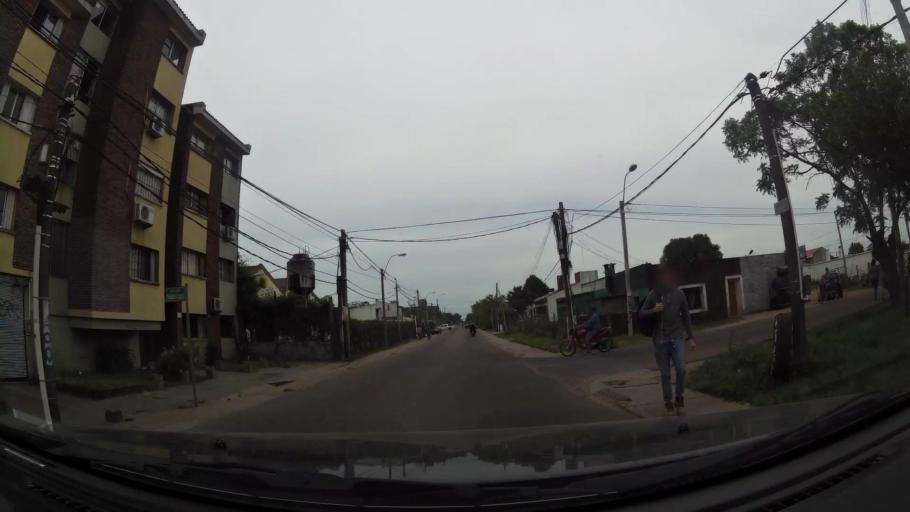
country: UY
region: Canelones
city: Las Piedras
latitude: -34.7292
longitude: -56.2277
